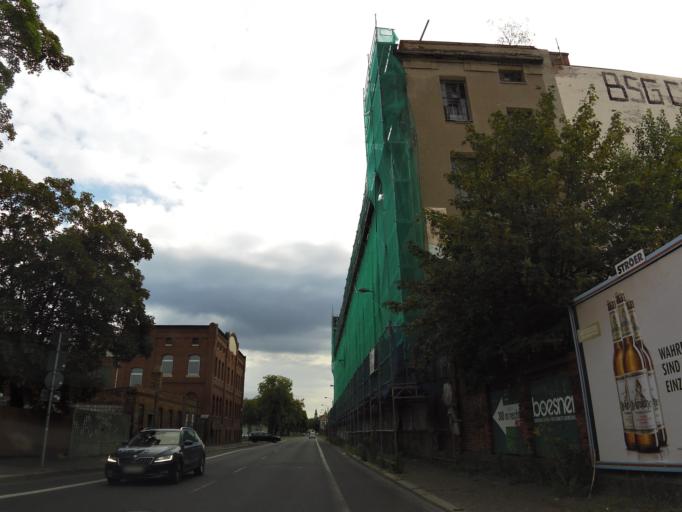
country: DE
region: Saxony
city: Leipzig
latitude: 51.3259
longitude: 12.3151
